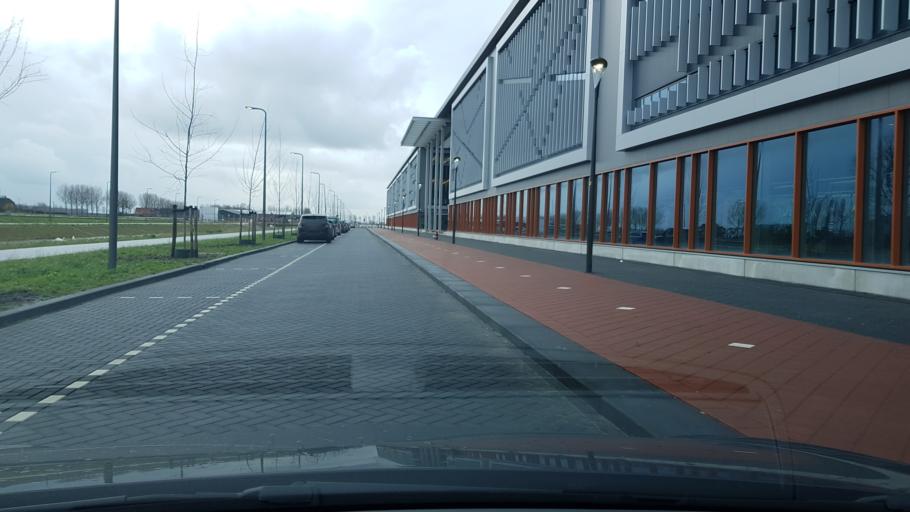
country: NL
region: North Holland
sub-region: Gemeente Haarlemmermeer
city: Hoofddorp
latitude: 52.2841
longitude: 4.6981
